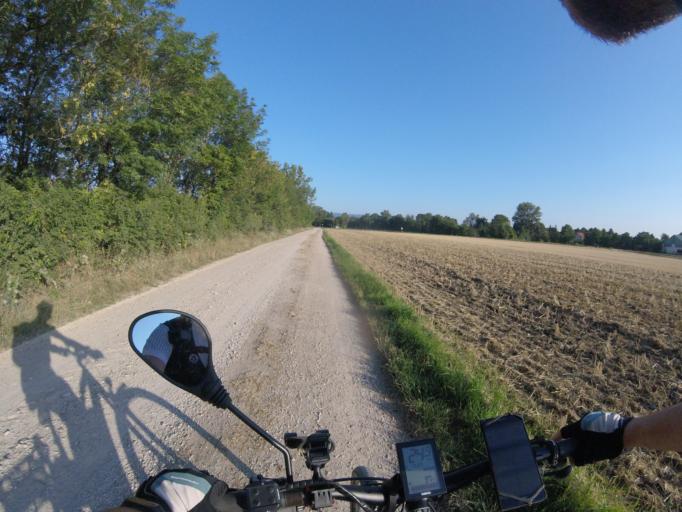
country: AT
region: Lower Austria
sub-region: Politischer Bezirk Baden
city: Trumau
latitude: 47.9889
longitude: 16.3432
